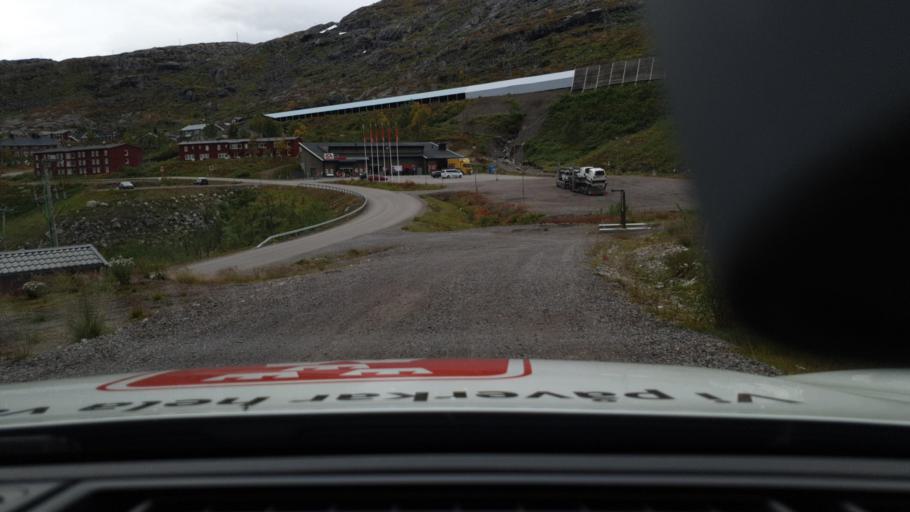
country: NO
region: Troms
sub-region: Lavangen
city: Tennevoll
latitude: 68.4301
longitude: 18.1178
